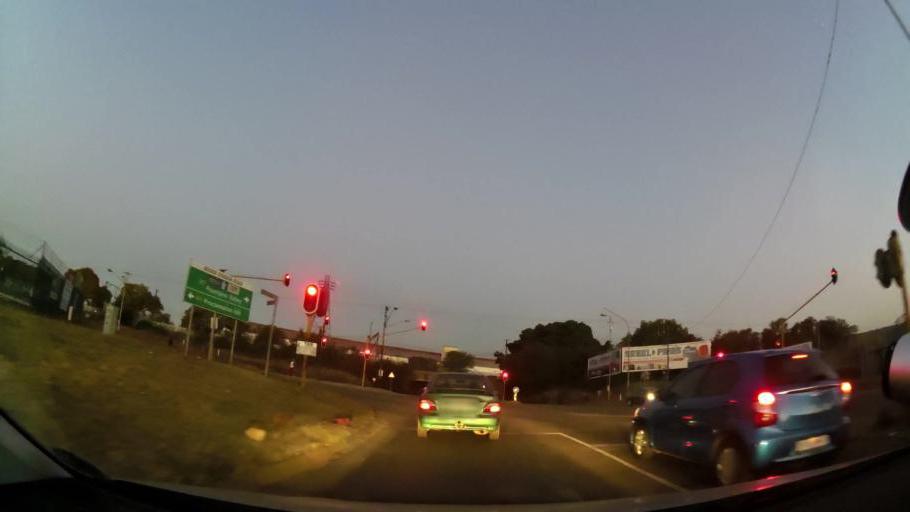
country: ZA
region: Gauteng
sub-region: City of Tshwane Metropolitan Municipality
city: Pretoria
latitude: -25.7629
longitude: 28.1424
